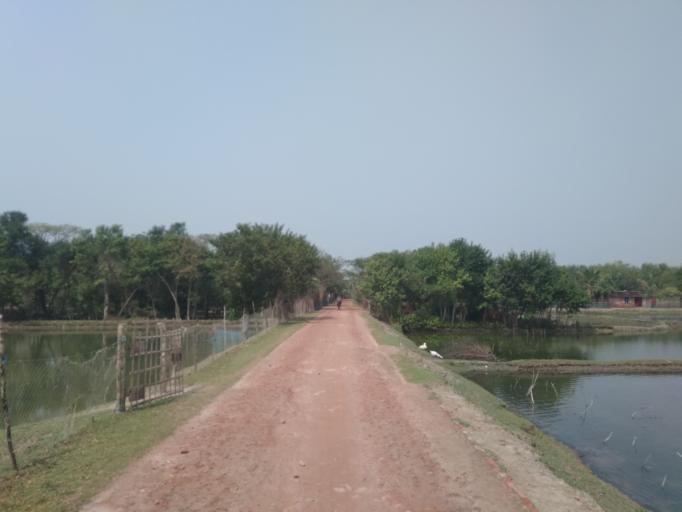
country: IN
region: West Bengal
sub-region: North 24 Parganas
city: Taki
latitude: 22.2974
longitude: 89.2701
